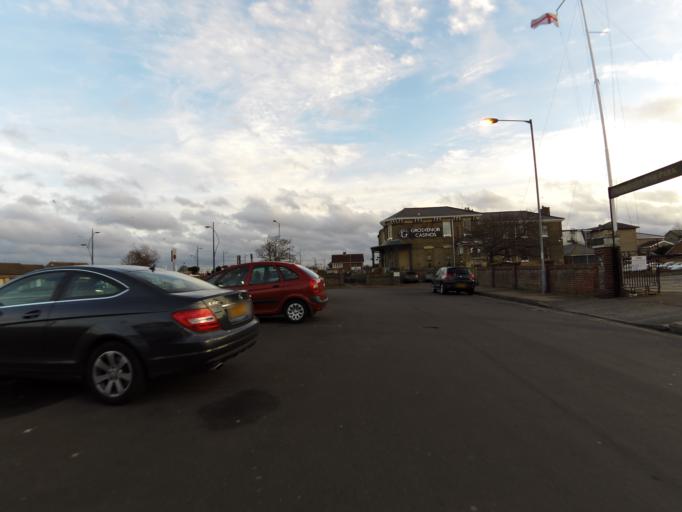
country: GB
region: England
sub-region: Norfolk
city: Great Yarmouth
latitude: 52.5995
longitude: 1.7353
